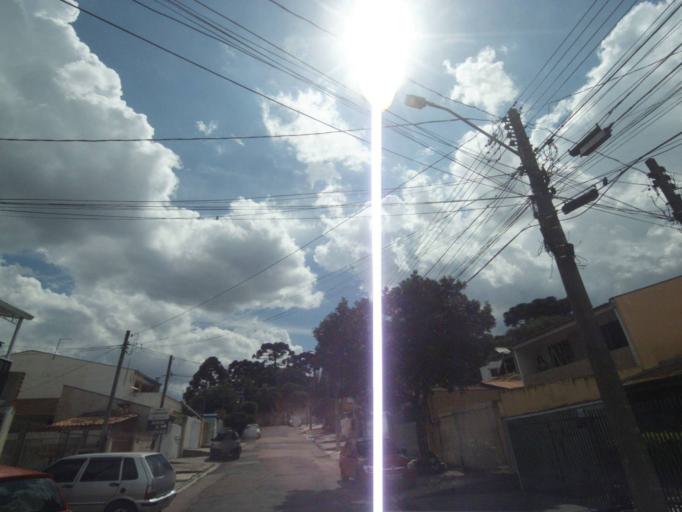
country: BR
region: Parana
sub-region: Curitiba
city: Curitiba
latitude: -25.4590
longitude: -49.3418
